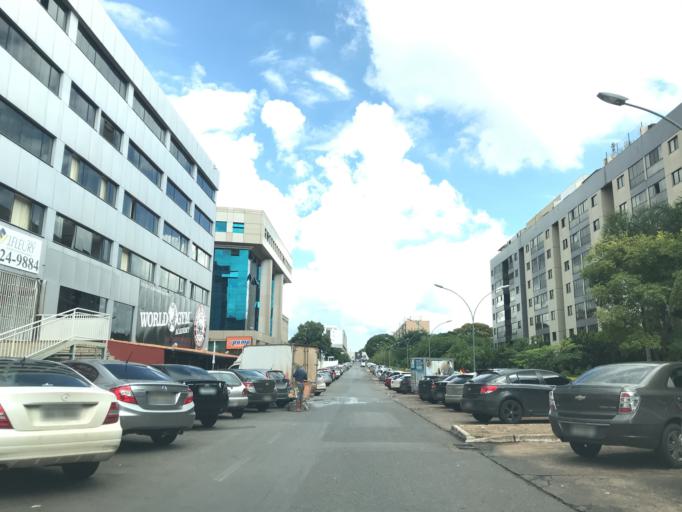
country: BR
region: Federal District
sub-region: Brasilia
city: Brasilia
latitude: -15.7559
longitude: -47.8928
